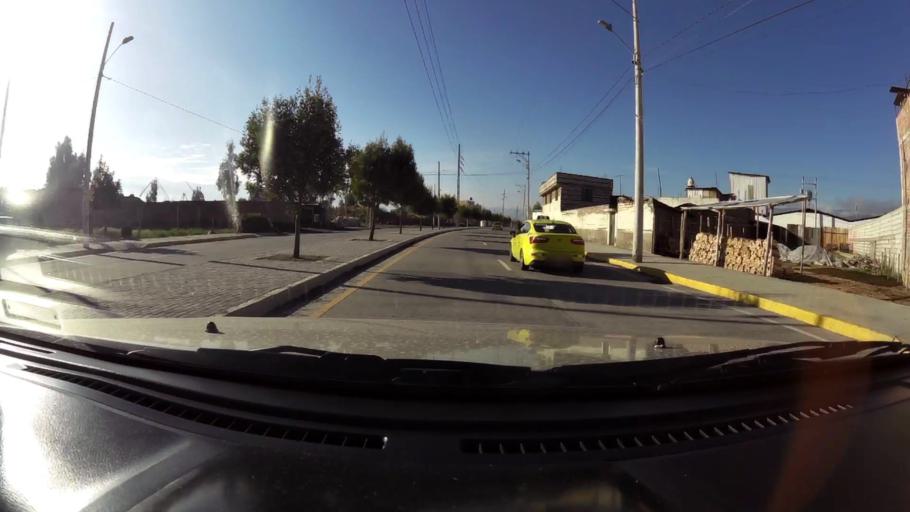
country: EC
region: Chimborazo
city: Riobamba
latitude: -1.6773
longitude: -78.6299
